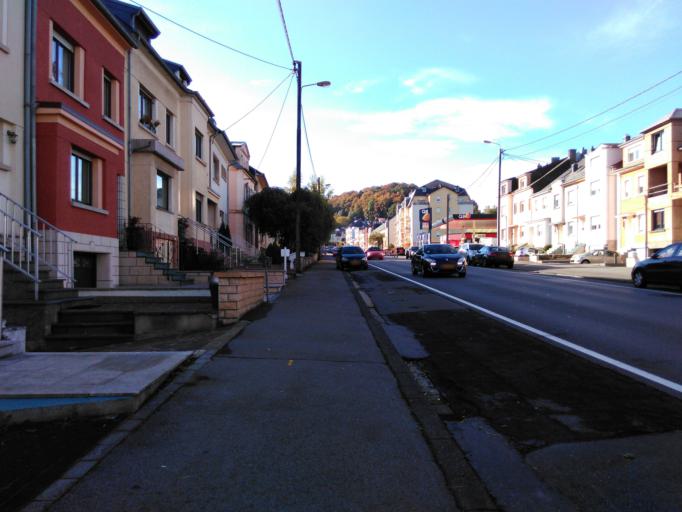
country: LU
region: Luxembourg
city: Belvaux
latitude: 49.5108
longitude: 5.9340
